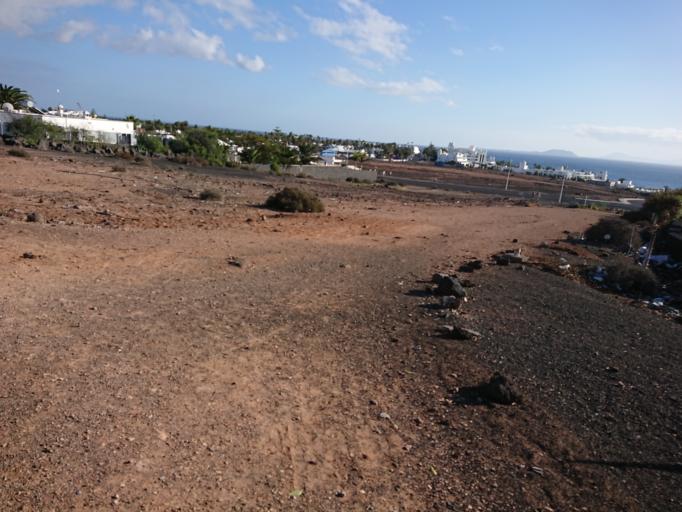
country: ES
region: Canary Islands
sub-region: Provincia de Las Palmas
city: Playa Blanca
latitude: 28.8649
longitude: -13.8461
